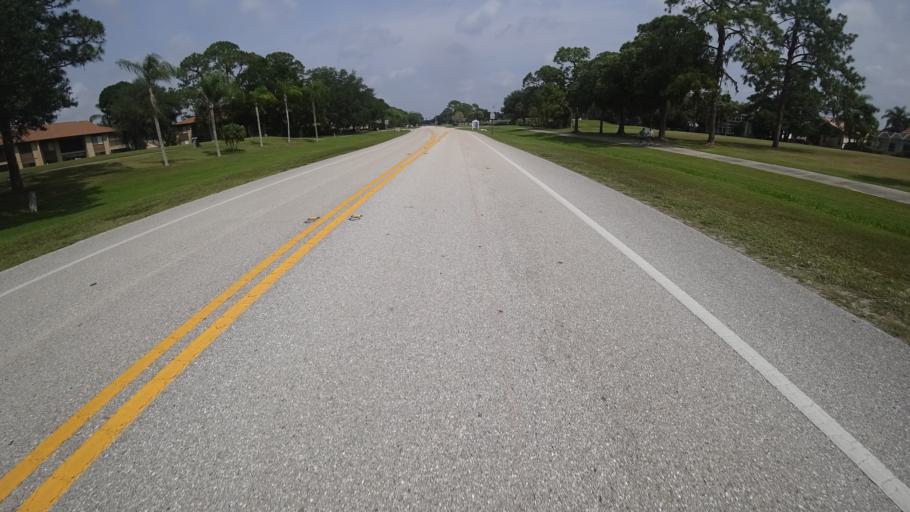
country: US
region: Florida
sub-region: Sarasota County
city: Desoto Lakes
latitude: 27.4085
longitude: -82.4877
